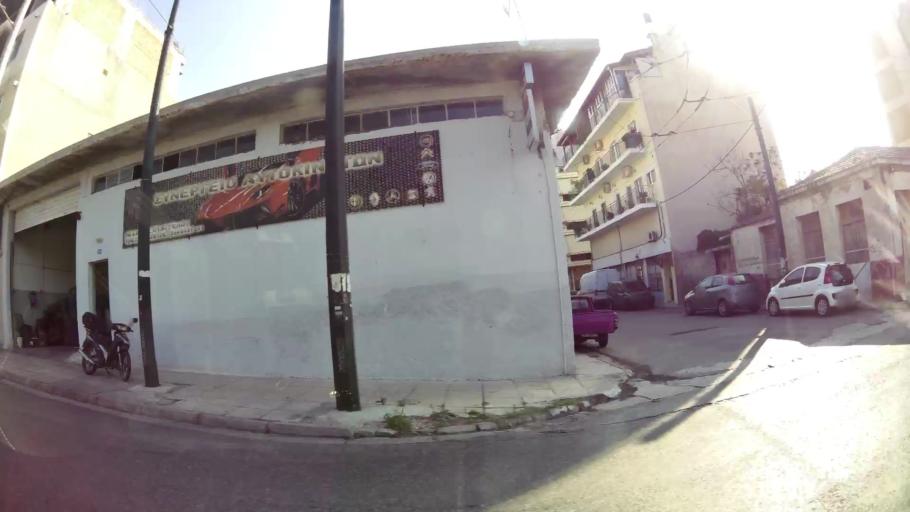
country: GR
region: Attica
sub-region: Nomos Piraios
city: Drapetsona
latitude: 37.9441
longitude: 23.6216
